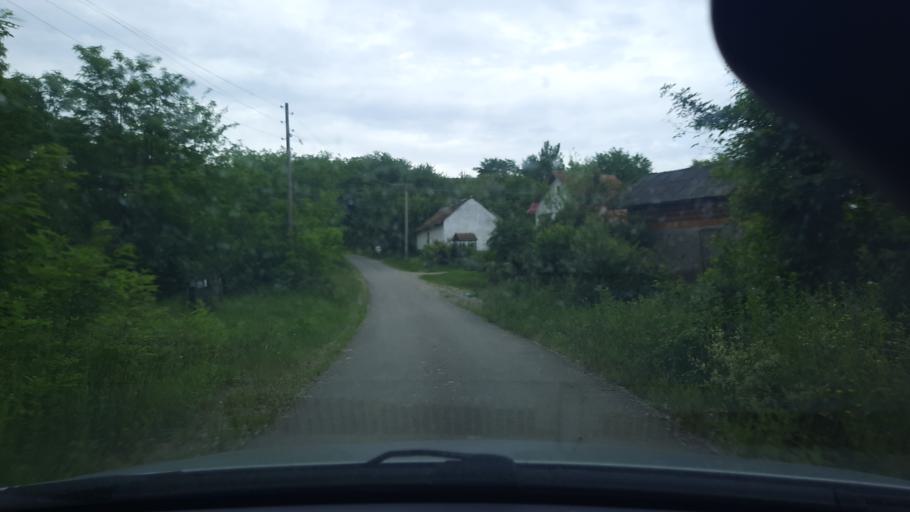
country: RS
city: Jarebice
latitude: 44.5102
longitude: 19.4729
